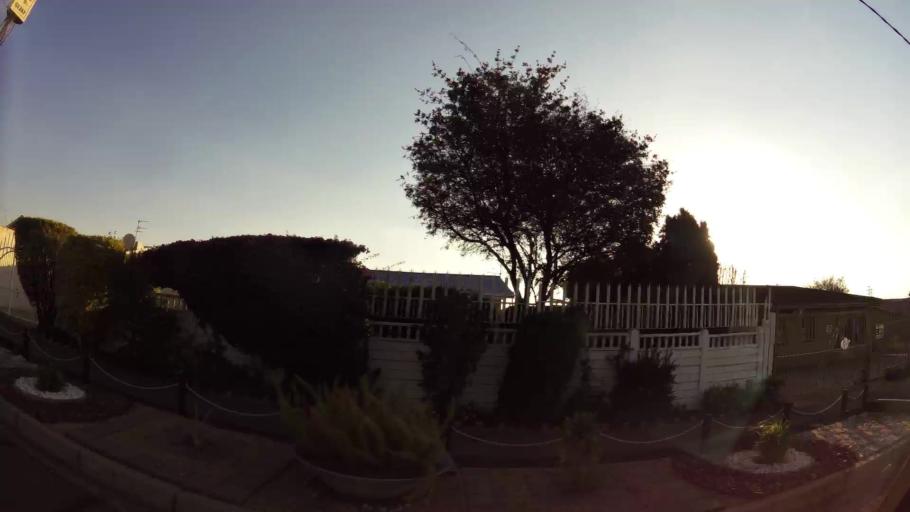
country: ZA
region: Gauteng
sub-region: City of Johannesburg Metropolitan Municipality
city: Johannesburg
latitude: -26.2532
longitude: 28.0072
